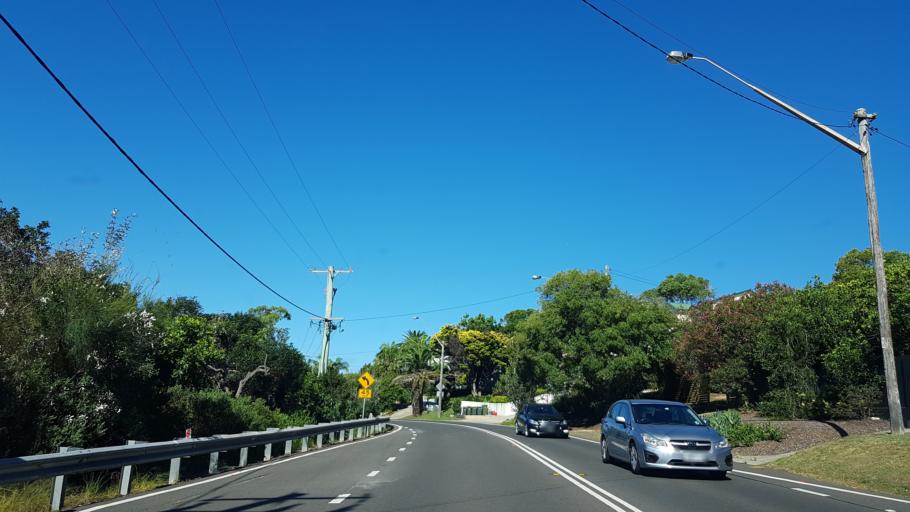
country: AU
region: New South Wales
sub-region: Pittwater
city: Bilgola Beach
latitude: -33.6421
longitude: 151.3306
